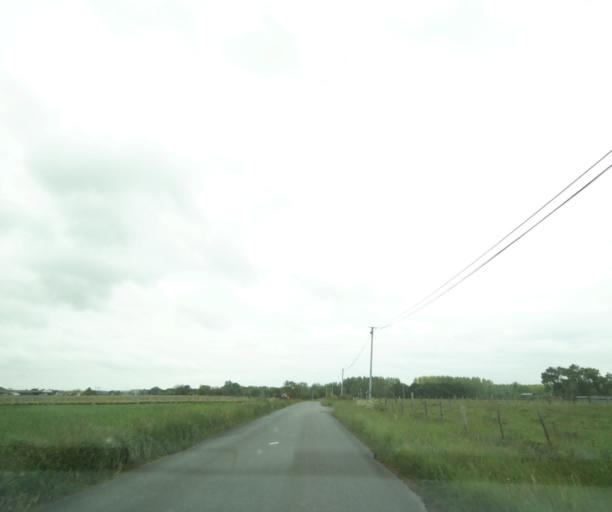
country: FR
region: Poitou-Charentes
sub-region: Departement de la Charente-Maritime
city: Chaniers
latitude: 45.7056
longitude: -0.5647
